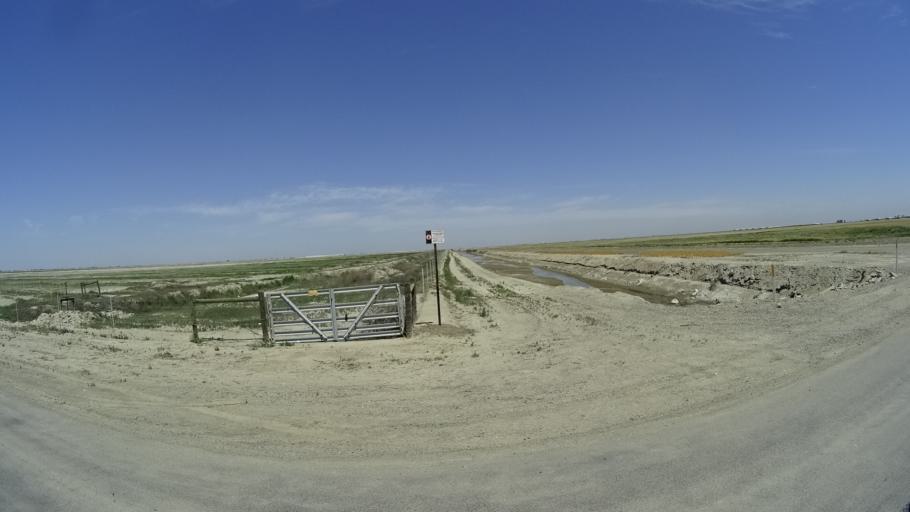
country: US
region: California
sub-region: Kings County
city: Corcoran
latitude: 36.1233
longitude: -119.6806
